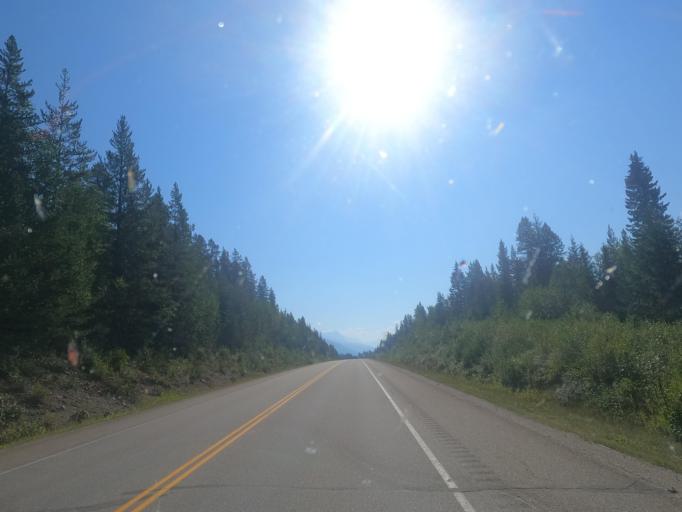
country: CA
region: Alberta
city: Jasper Park Lodge
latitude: 52.9765
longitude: -118.9647
